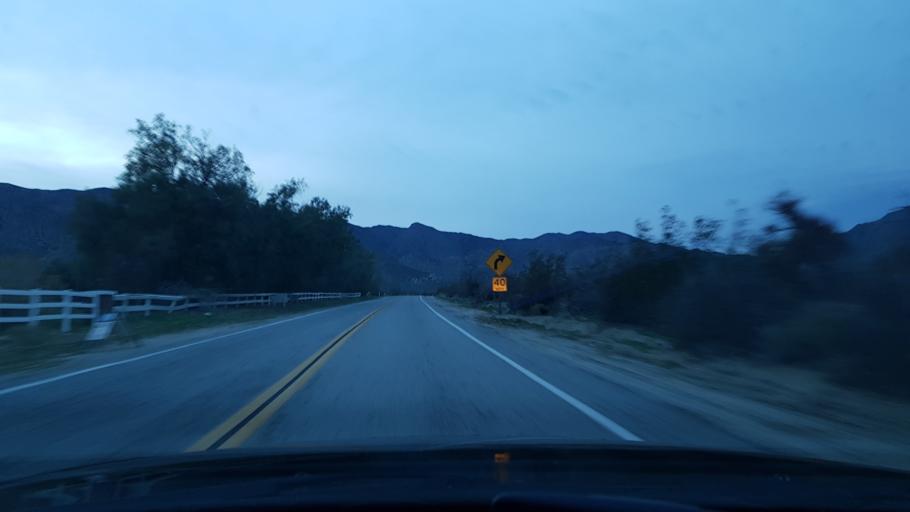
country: US
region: California
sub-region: San Diego County
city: Pine Valley
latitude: 32.9799
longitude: -116.4368
